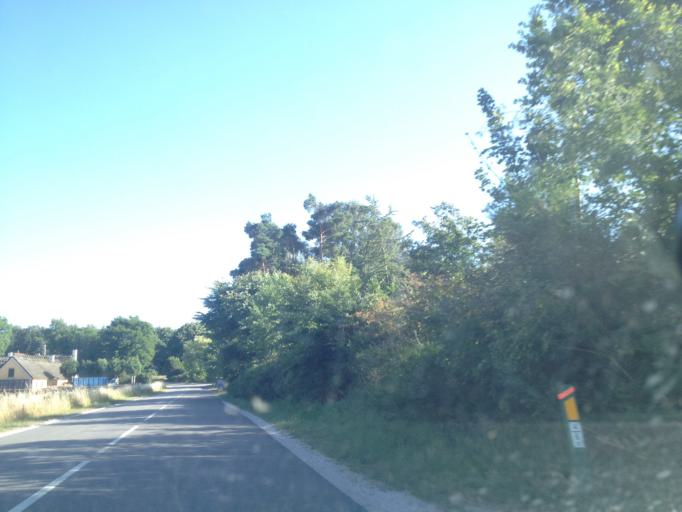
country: DK
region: Capital Region
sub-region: Gribskov Kommune
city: Helsinge
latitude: 56.0491
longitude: 12.1096
